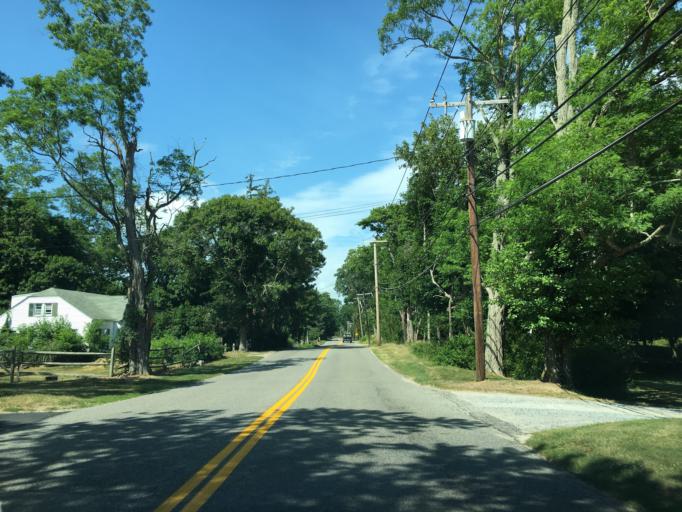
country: US
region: New York
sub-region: Suffolk County
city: Shelter Island Heights
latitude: 41.0702
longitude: -72.3613
